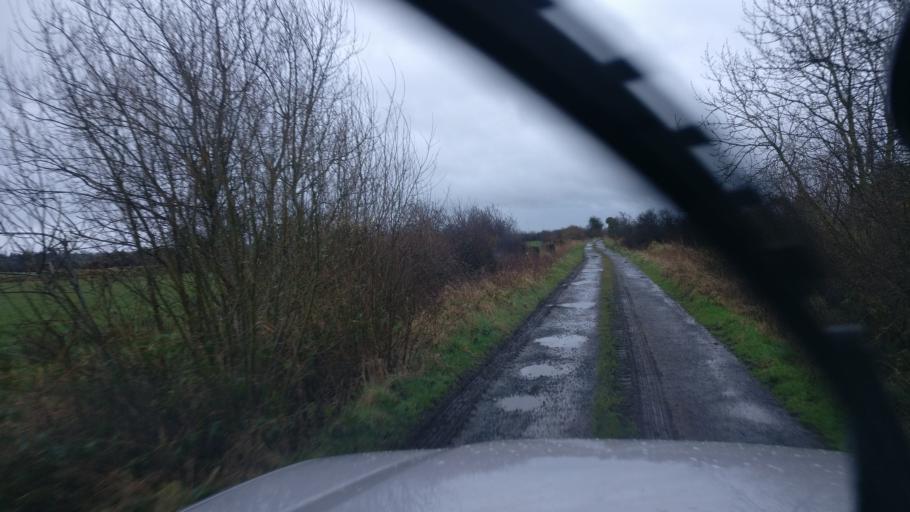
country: IE
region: Connaught
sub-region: County Galway
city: Ballinasloe
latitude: 53.2514
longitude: -8.3320
